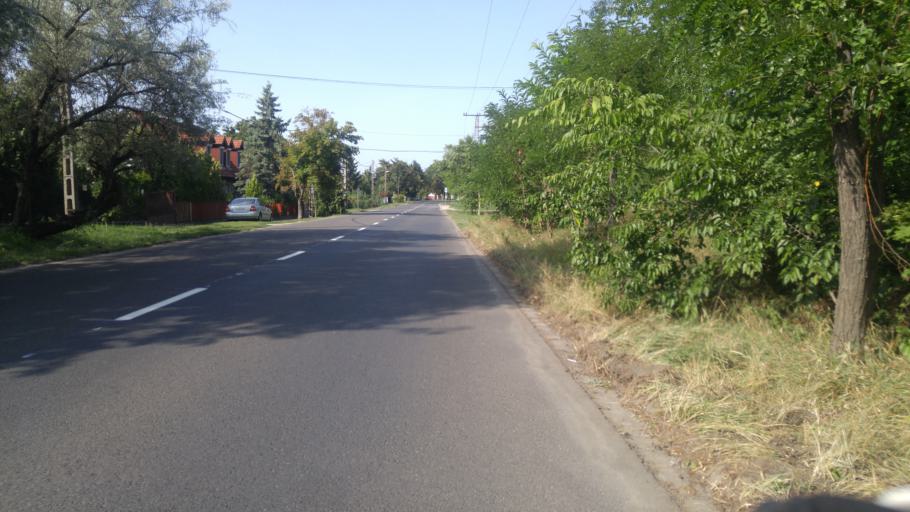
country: HU
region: Budapest
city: Budapest XVII. keruelet
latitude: 47.4626
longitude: 19.2468
